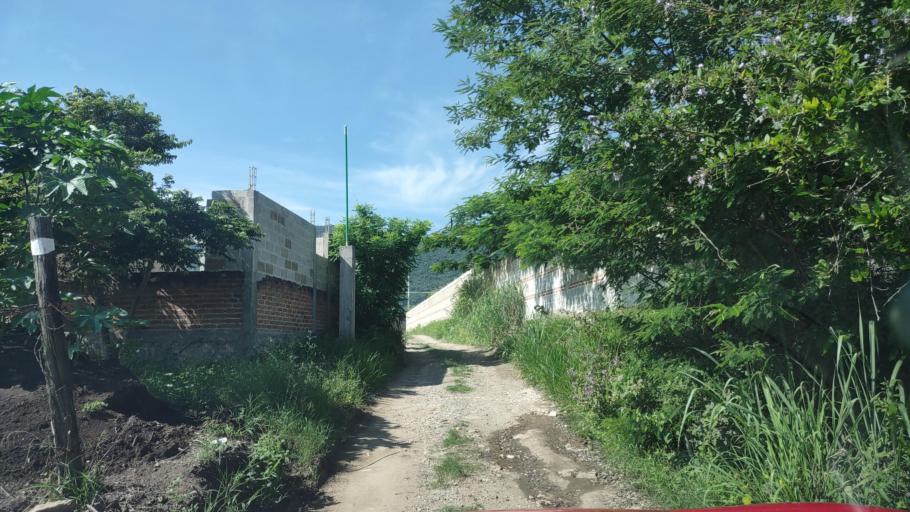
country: MX
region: Veracruz
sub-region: Emiliano Zapata
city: Dos Rios
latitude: 19.4310
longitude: -96.8003
